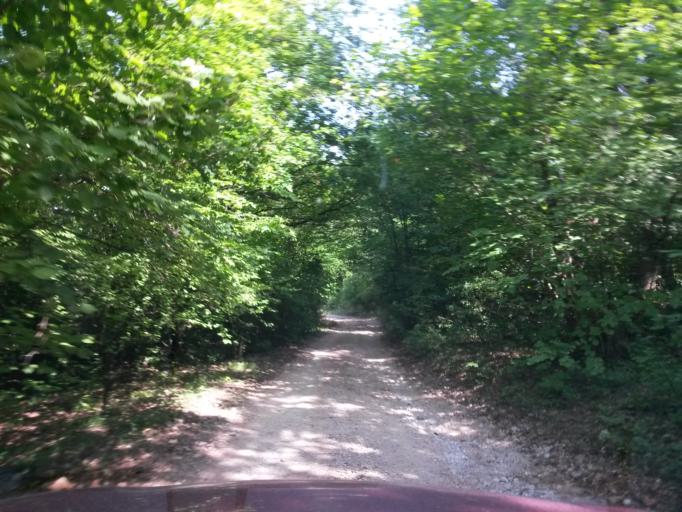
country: SK
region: Kosicky
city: Moldava nad Bodvou
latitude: 48.6469
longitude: 20.9642
